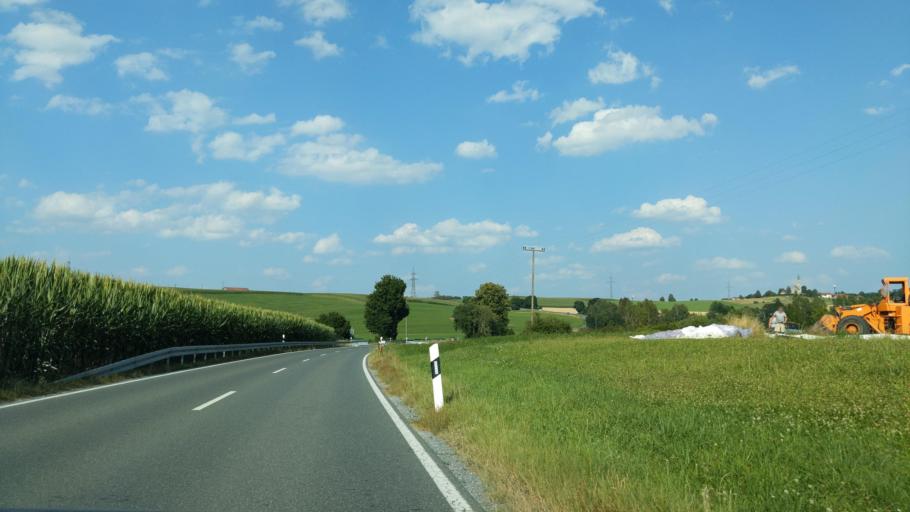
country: DE
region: Bavaria
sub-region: Upper Bavaria
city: Bruck
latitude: 48.0227
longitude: 11.9080
